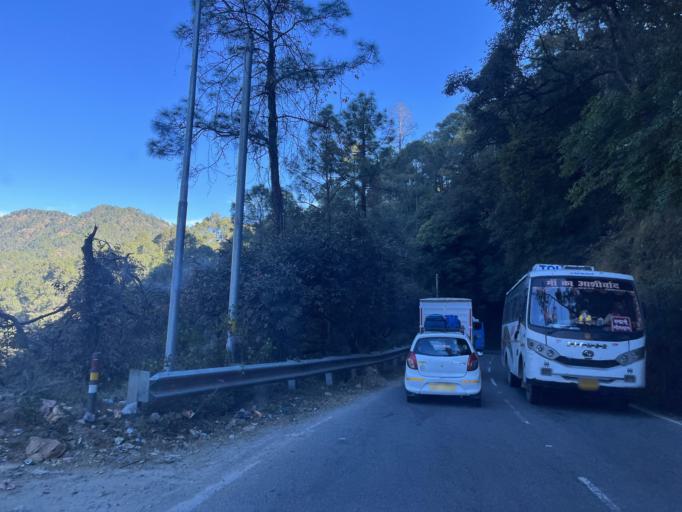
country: IN
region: Uttarakhand
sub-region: Naini Tal
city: Bhowali
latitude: 29.3951
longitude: 79.5114
